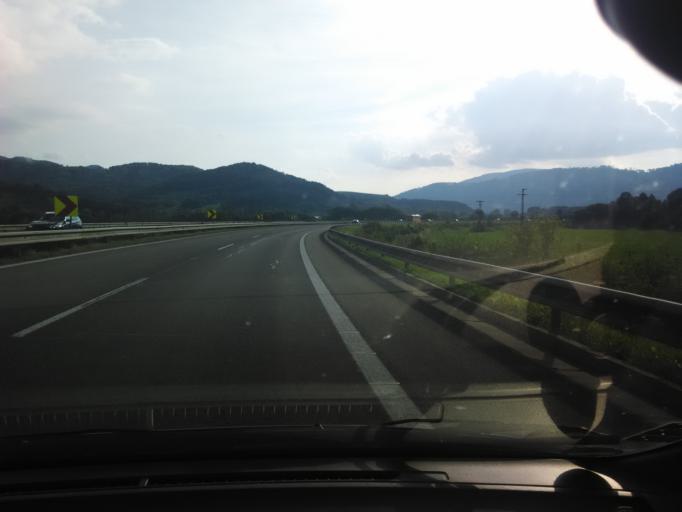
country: SK
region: Banskobystricky
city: Zarnovica
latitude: 48.4778
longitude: 18.7292
